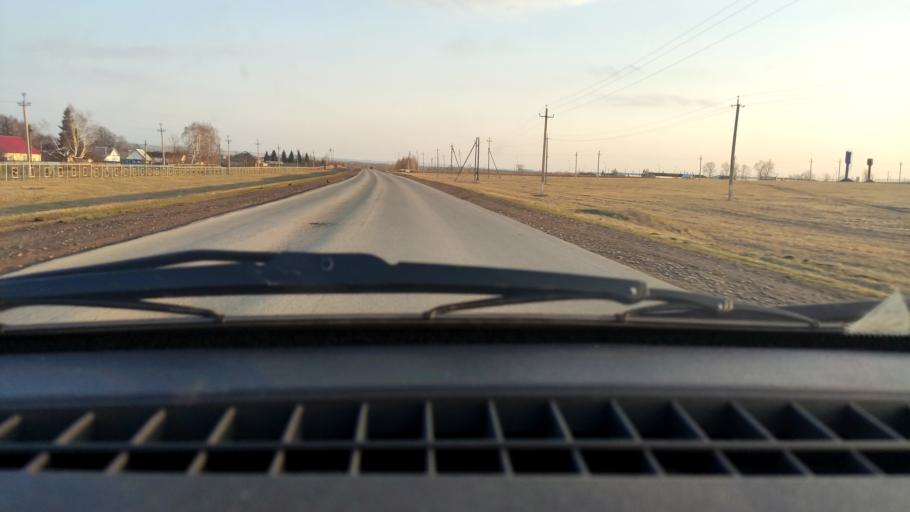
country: RU
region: Bashkortostan
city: Davlekanovo
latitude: 54.3811
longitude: 55.1958
